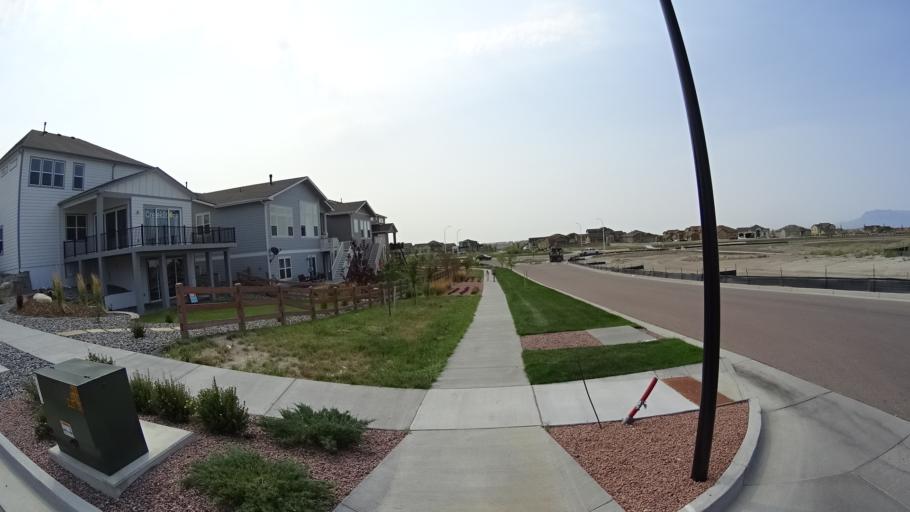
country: US
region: Colorado
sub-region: El Paso County
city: Black Forest
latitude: 38.9723
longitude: -104.7252
